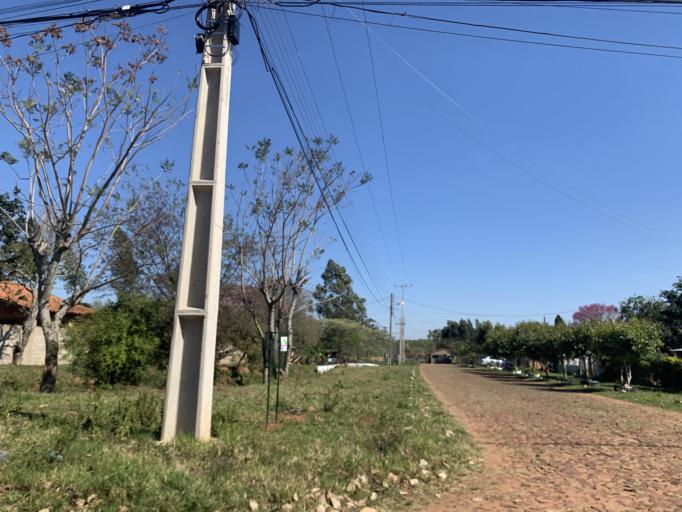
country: PY
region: Misiones
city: San Juan Bautista
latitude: -26.6625
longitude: -57.1406
